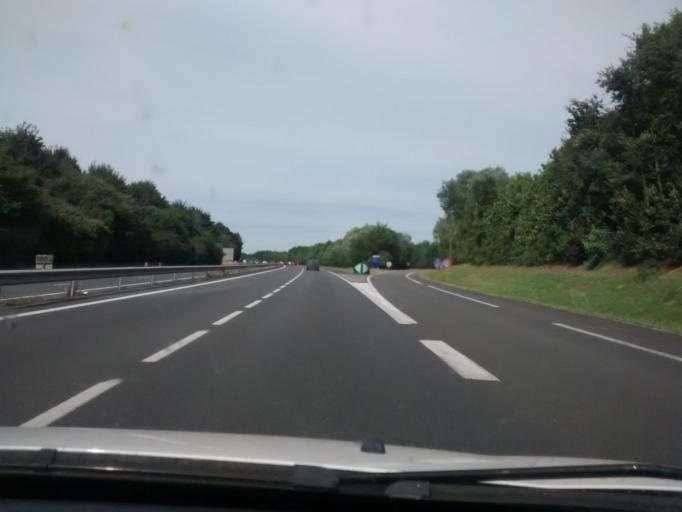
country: FR
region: Pays de la Loire
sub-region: Departement de la Sarthe
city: Pruille-le-Chetif
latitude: 48.0008
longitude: 0.0921
